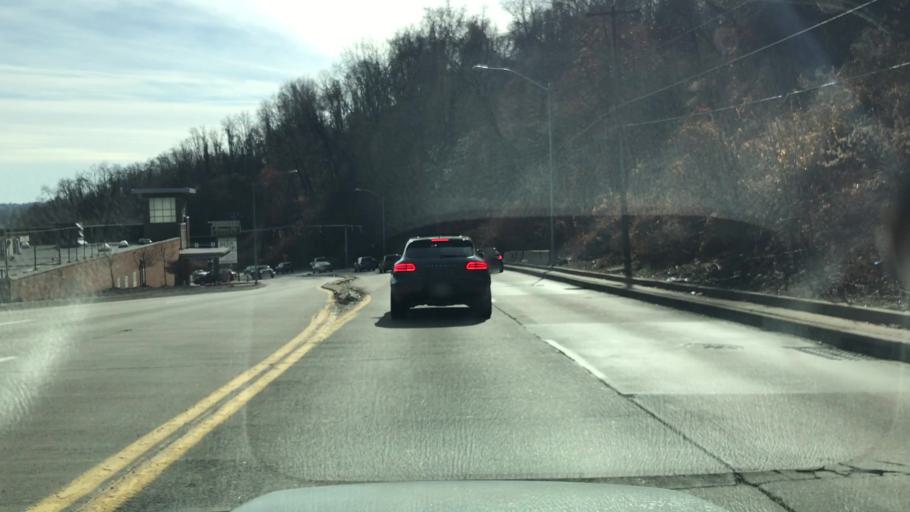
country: US
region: Pennsylvania
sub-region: Allegheny County
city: Homestead
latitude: 40.4174
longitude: -79.9259
